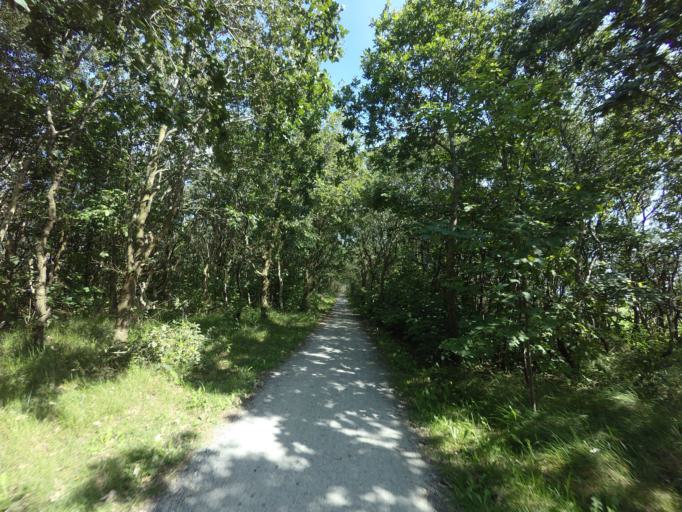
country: NL
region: Friesland
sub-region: Gemeente Ameland
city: Hollum
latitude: 53.4438
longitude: 5.6678
